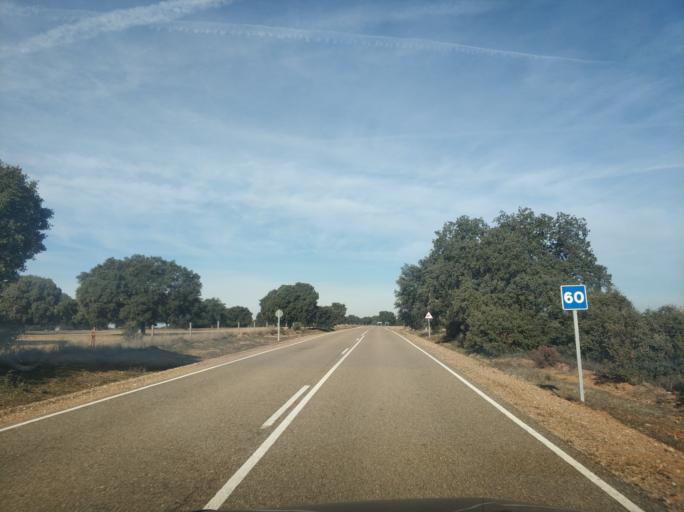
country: ES
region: Castille and Leon
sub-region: Provincia de Salamanca
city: Parada de Arriba
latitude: 41.0011
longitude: -5.8285
